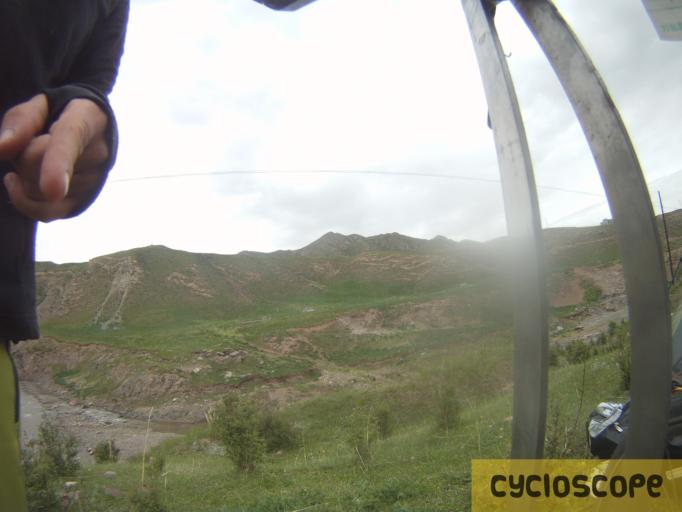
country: CN
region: Gansu Sheng
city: Nanfeng
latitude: 38.2079
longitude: 100.9370
